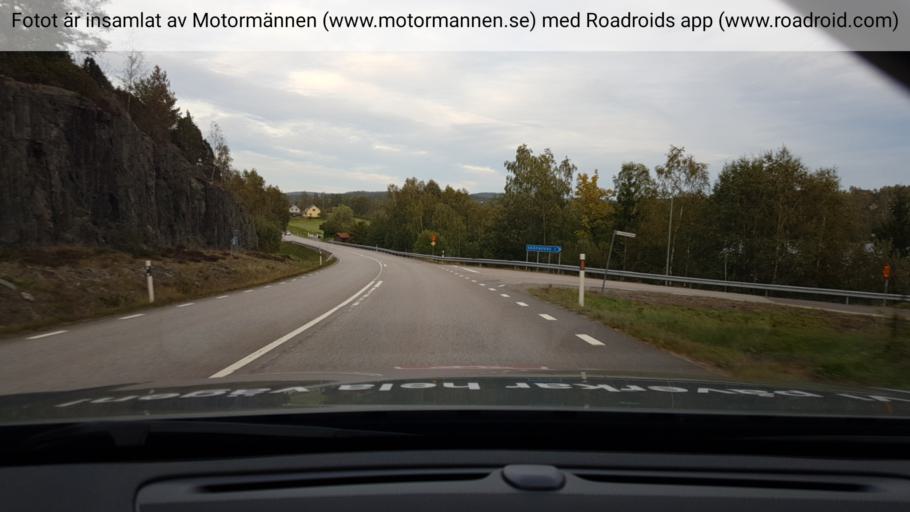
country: SE
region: Vaestra Goetaland
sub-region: Bengtsfors Kommun
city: Billingsfors
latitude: 59.0291
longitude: 12.3009
